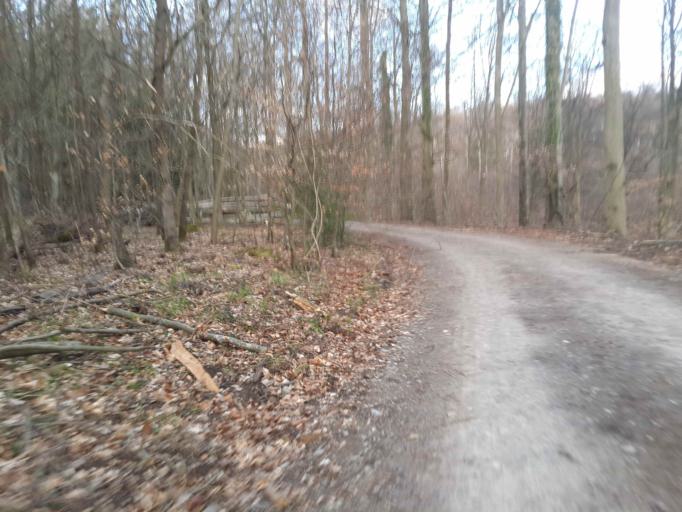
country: DE
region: Baden-Wuerttemberg
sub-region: Regierungsbezirk Stuttgart
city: Ittlingen
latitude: 49.2322
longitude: 8.9506
